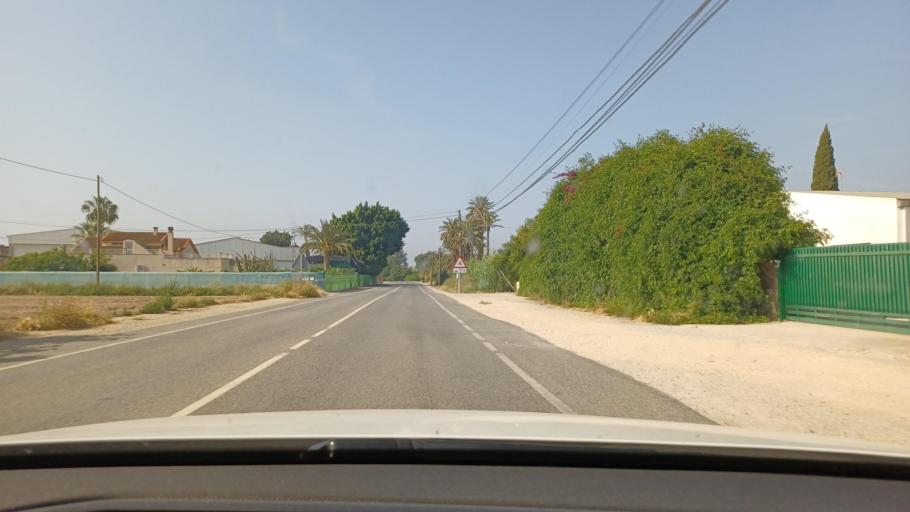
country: ES
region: Valencia
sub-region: Provincia de Alicante
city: Elche
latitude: 38.2260
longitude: -0.7184
